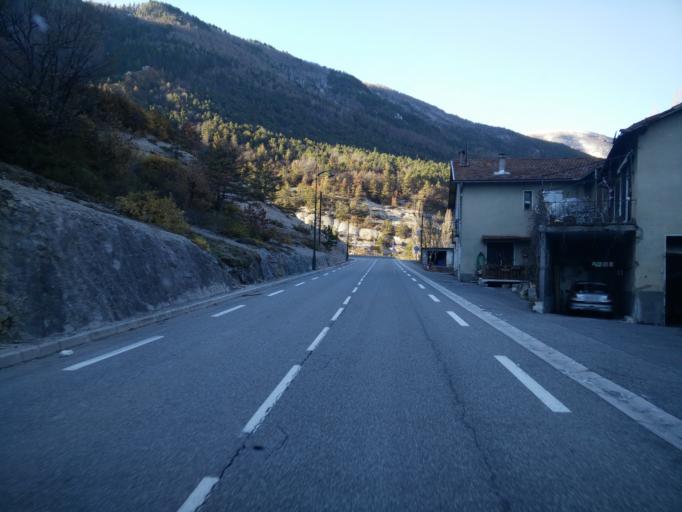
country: FR
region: Provence-Alpes-Cote d'Azur
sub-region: Departement des Alpes-de-Haute-Provence
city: Annot
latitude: 43.9554
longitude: 6.6860
